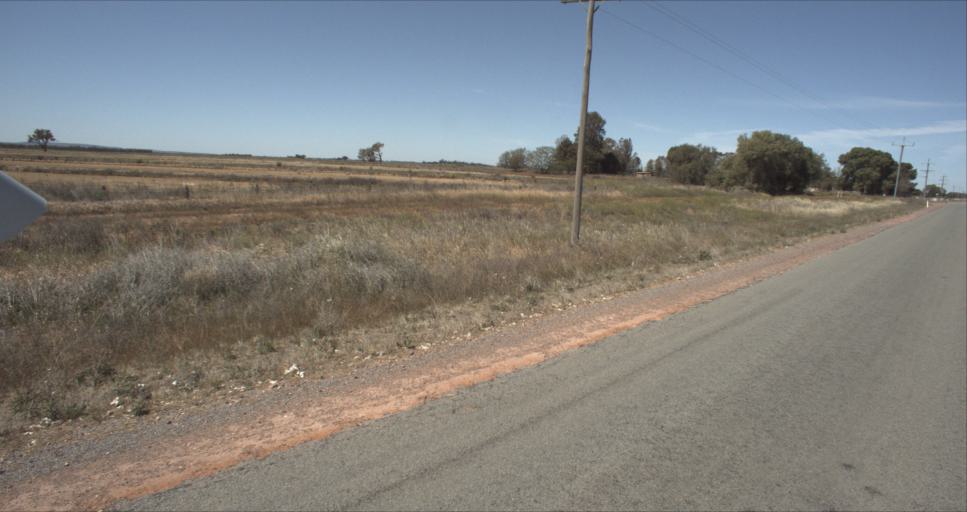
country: AU
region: New South Wales
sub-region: Leeton
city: Leeton
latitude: -34.4393
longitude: 146.2981
